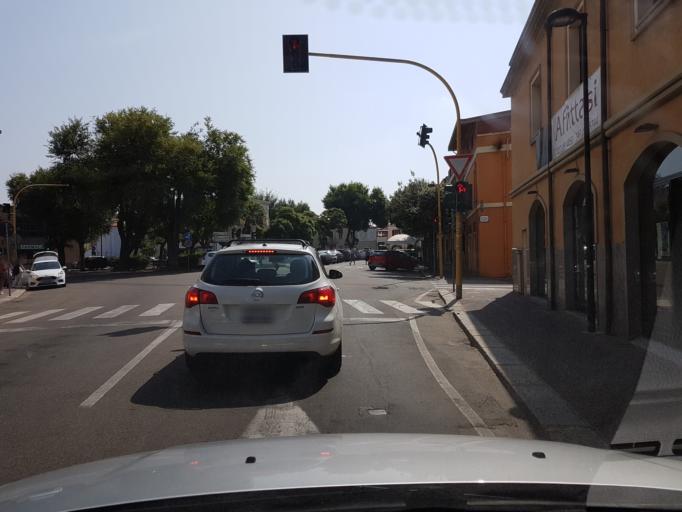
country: IT
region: Sardinia
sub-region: Provincia di Oristano
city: Oristano
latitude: 39.9053
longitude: 8.5958
